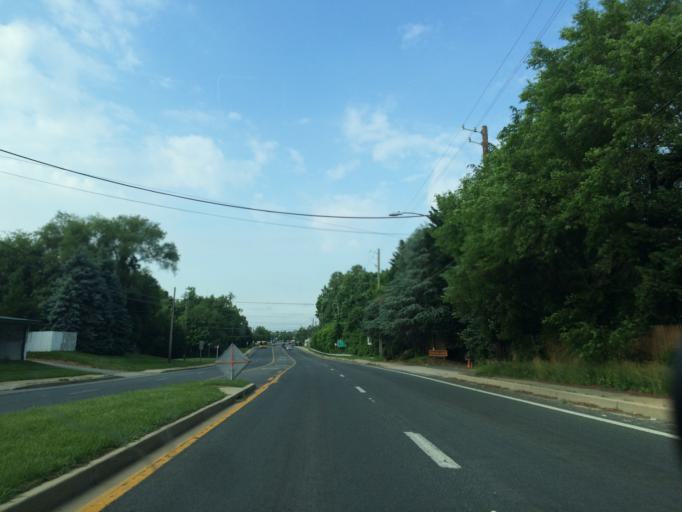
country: US
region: Maryland
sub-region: Montgomery County
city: Cloverly
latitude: 39.1149
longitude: -76.9929
